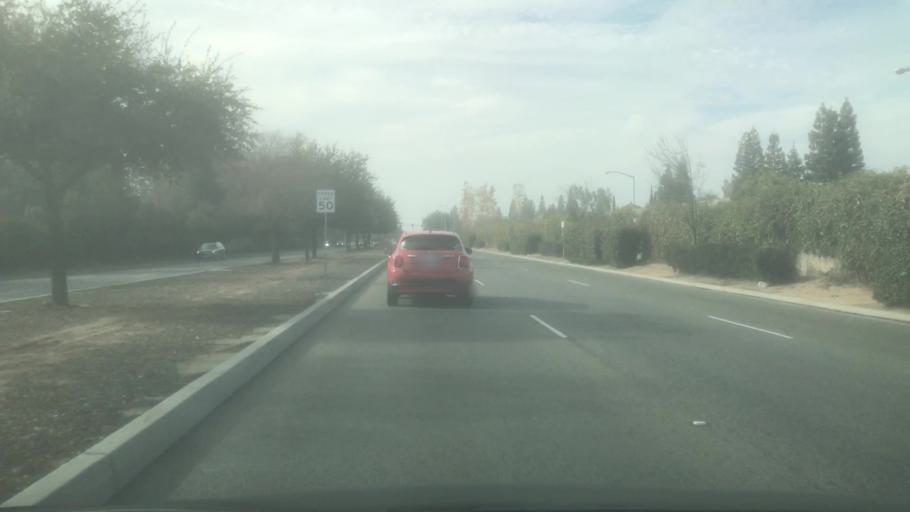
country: US
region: California
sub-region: Fresno County
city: Fresno
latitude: 36.8373
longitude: -119.8318
